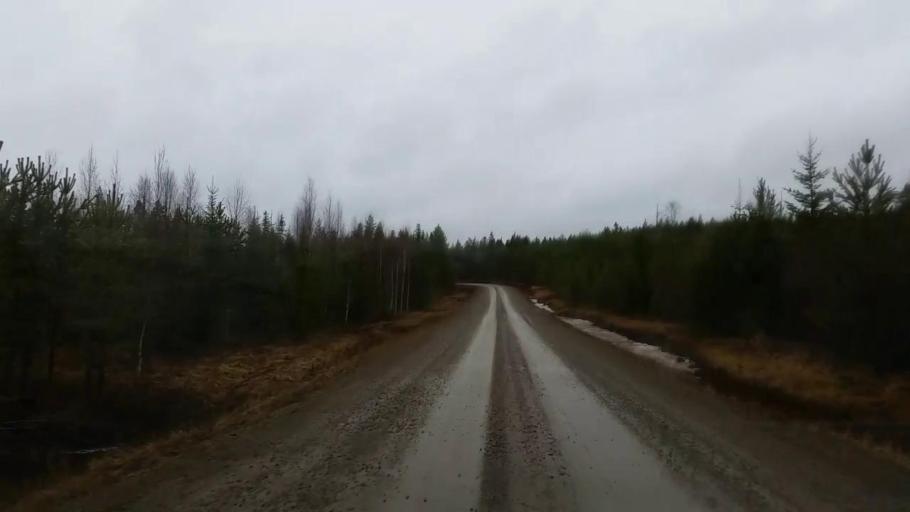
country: SE
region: Gaevleborg
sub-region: Ljusdals Kommun
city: Farila
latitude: 62.1157
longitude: 15.6894
